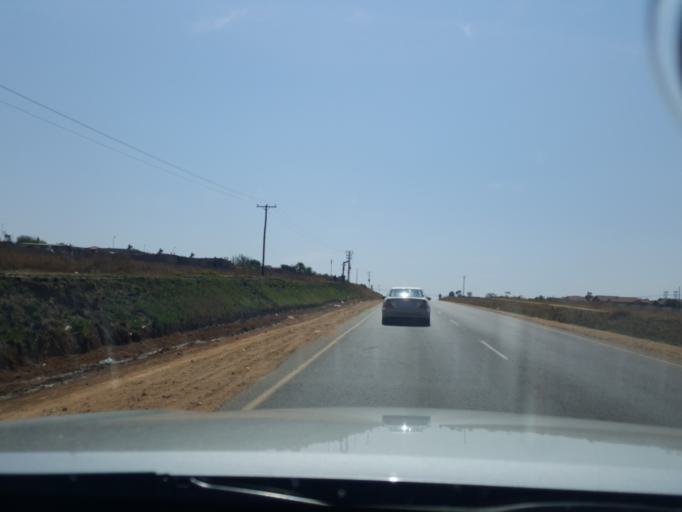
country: ZA
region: Gauteng
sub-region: City of Johannesburg Metropolitan Municipality
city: Midrand
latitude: -25.9140
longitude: 28.1003
